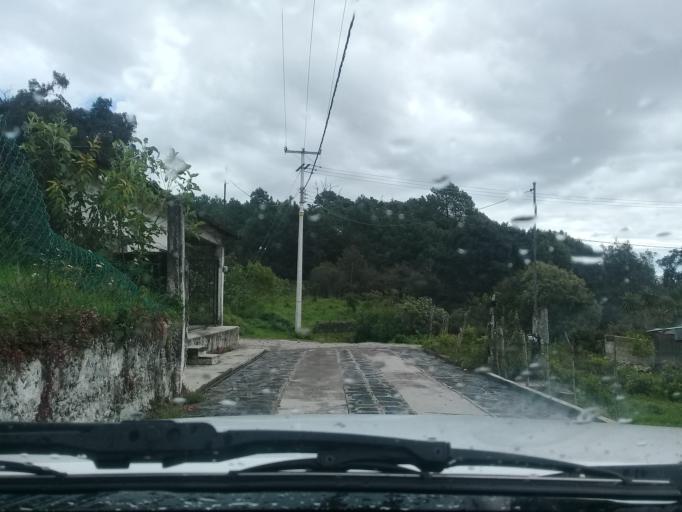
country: MX
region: Veracruz
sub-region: Acajete
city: La Joya
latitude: 19.6163
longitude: -97.0062
